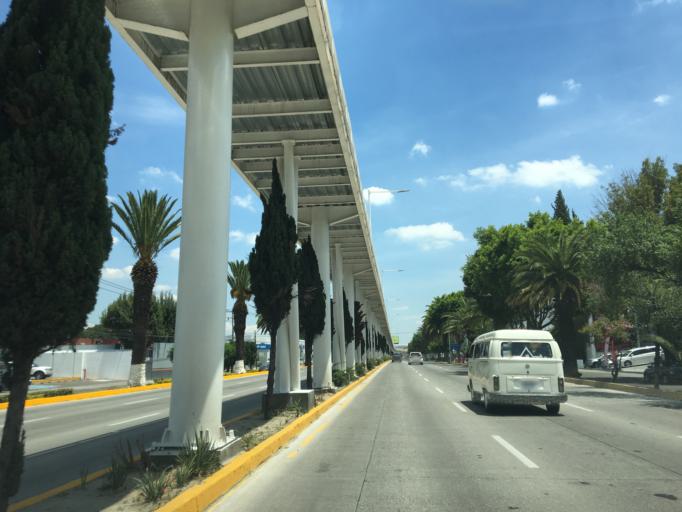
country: MX
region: Puebla
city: Puebla
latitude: 19.0681
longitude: -98.2247
